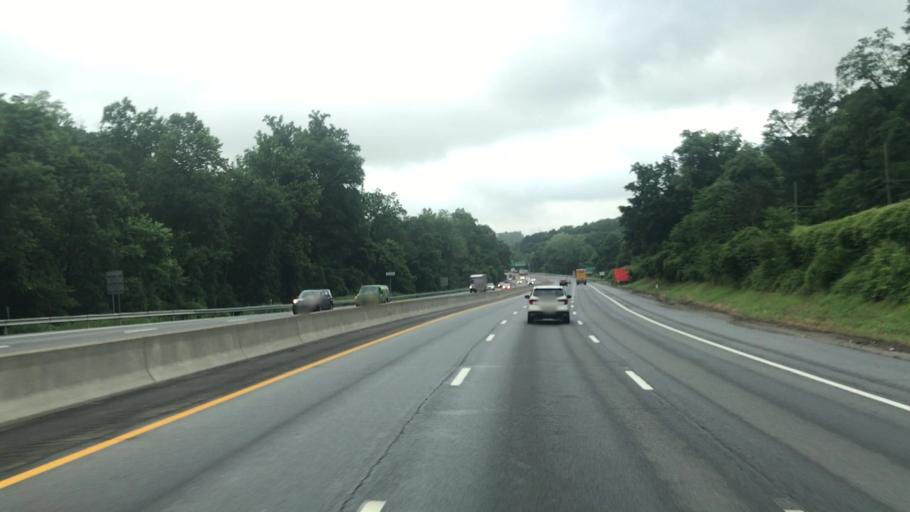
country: US
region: New York
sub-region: Westchester County
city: Greenburgh
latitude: 41.0345
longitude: -73.8397
